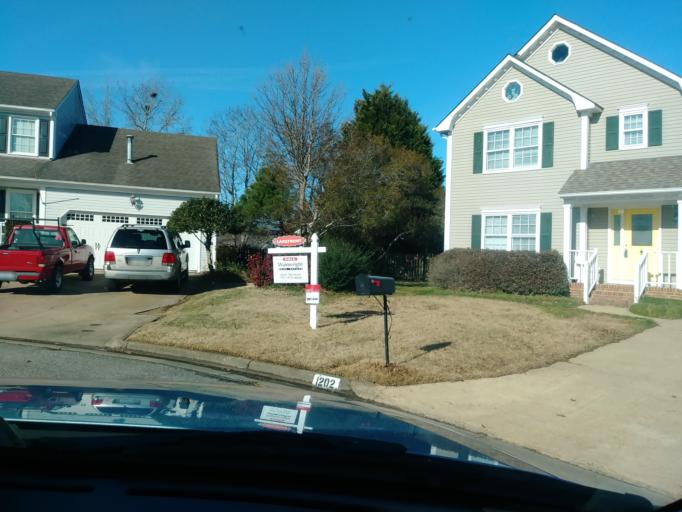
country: US
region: Virginia
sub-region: City of Chesapeake
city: Chesapeake
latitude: 36.7548
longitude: -76.2100
